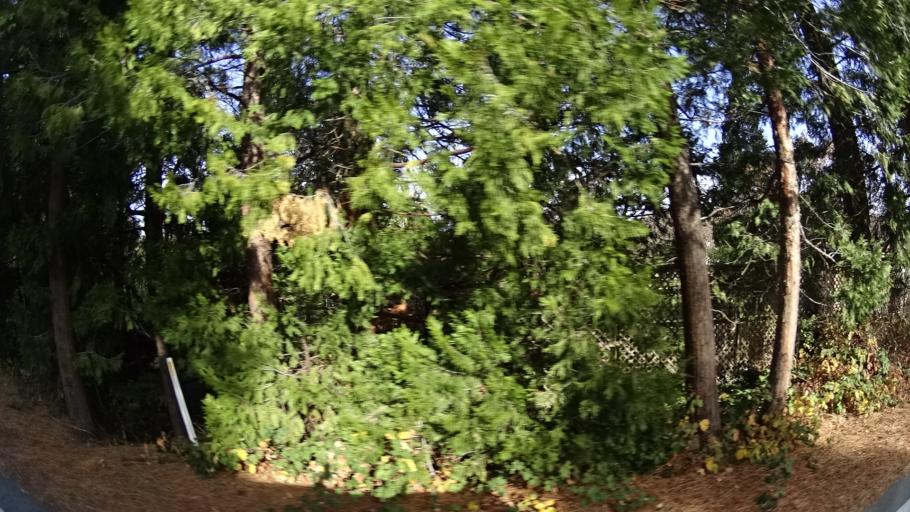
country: US
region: California
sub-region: Siskiyou County
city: Weed
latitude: 41.4072
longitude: -122.4315
